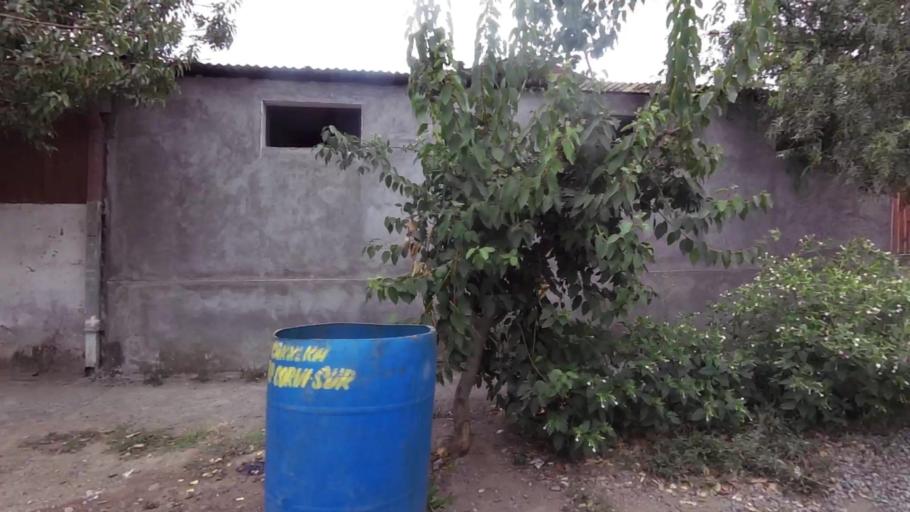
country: CL
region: O'Higgins
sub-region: Provincia de Cachapoal
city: Graneros
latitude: -34.0758
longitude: -70.7269
